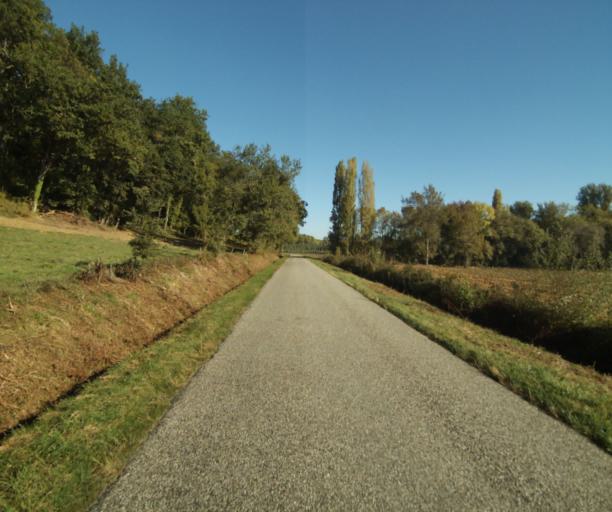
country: FR
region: Midi-Pyrenees
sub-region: Departement du Gers
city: Vic-Fezensac
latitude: 43.8243
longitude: 0.2885
